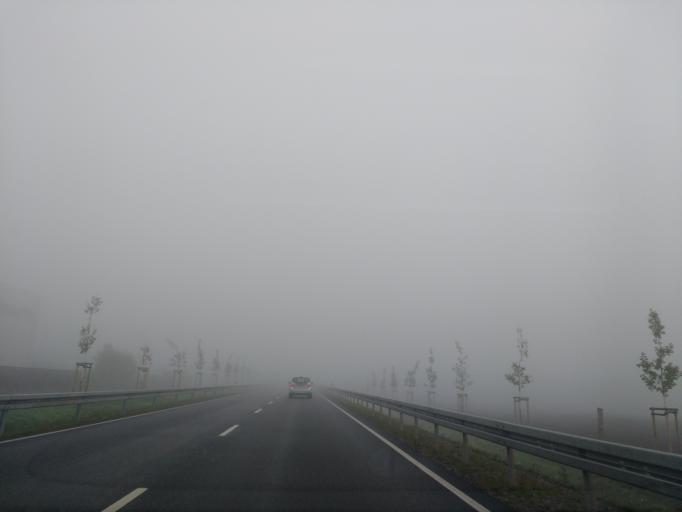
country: DE
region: Saxony-Anhalt
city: Halle (Saale)
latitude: 51.4851
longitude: 12.0179
